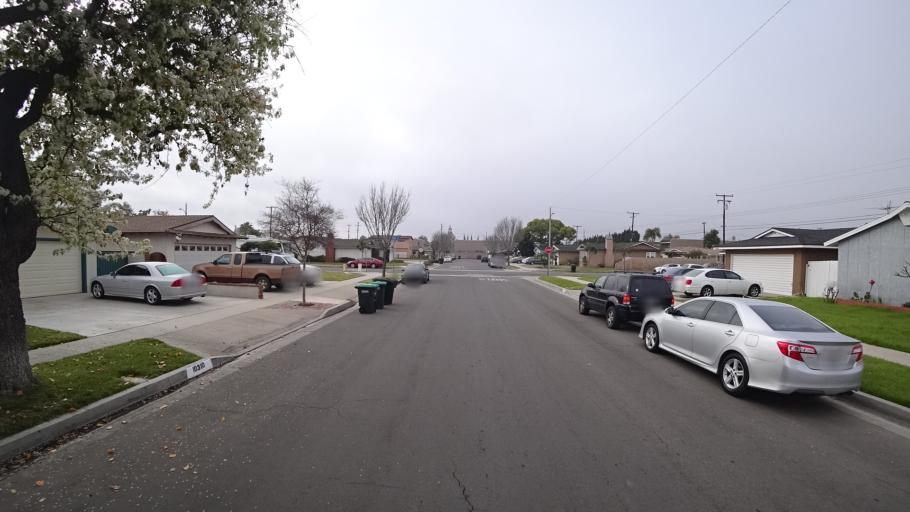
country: US
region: California
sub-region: Orange County
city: Stanton
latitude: 33.8127
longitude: -117.9994
